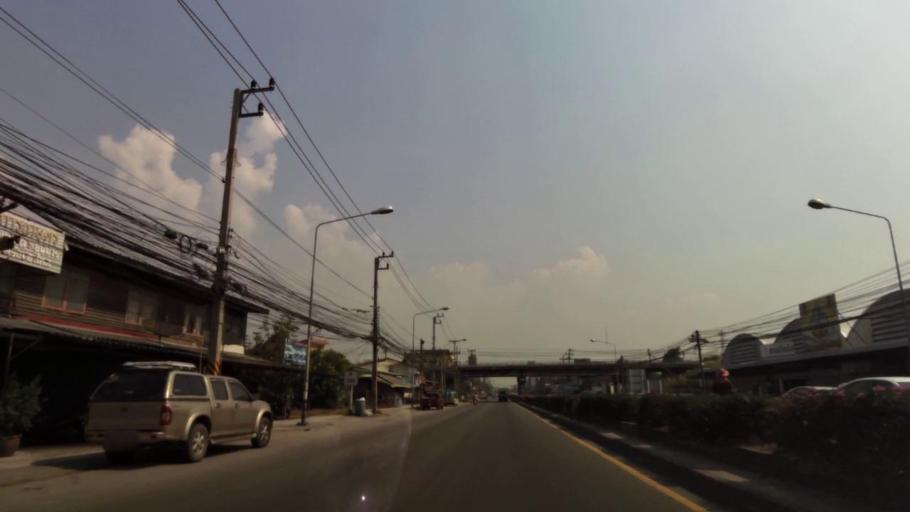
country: TH
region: Chon Buri
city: Chon Buri
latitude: 13.3523
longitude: 101.0066
